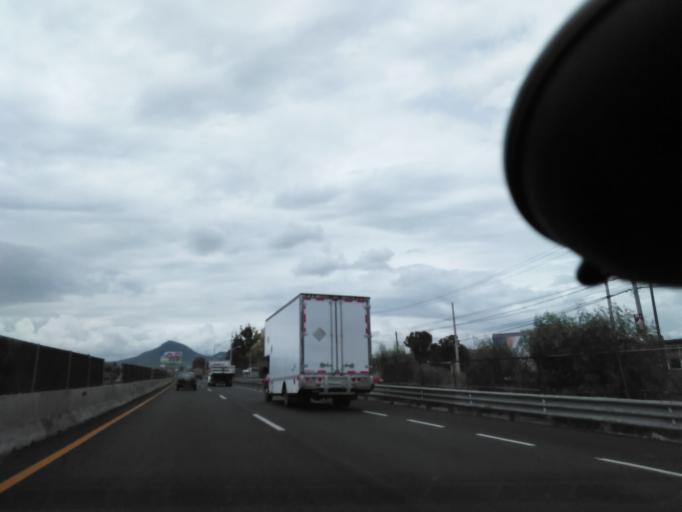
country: MX
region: Morelos
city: San Pedro Xalpa
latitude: 19.8175
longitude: -99.2001
